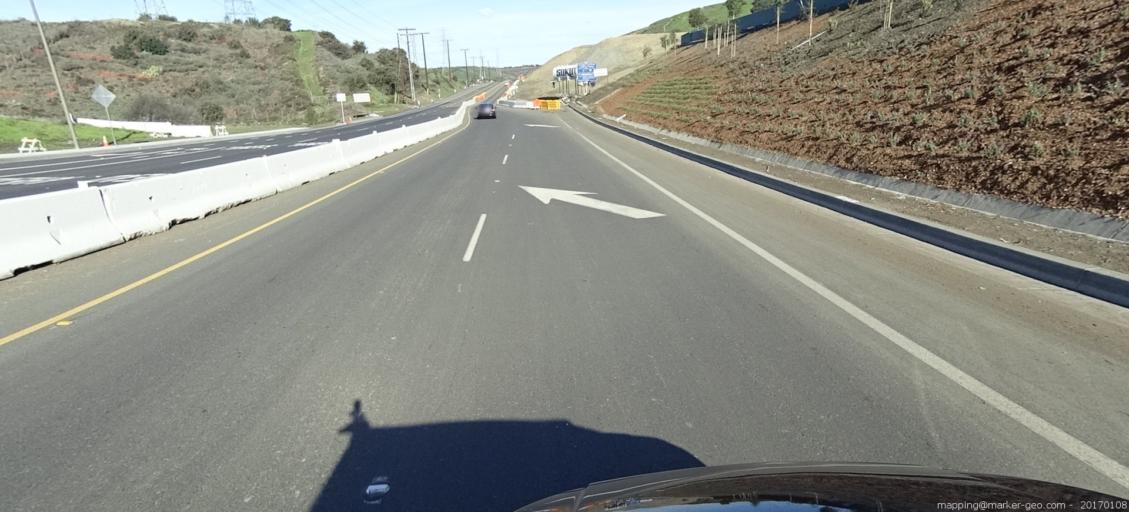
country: US
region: California
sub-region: Orange County
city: San Juan Capistrano
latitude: 33.5013
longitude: -117.6188
